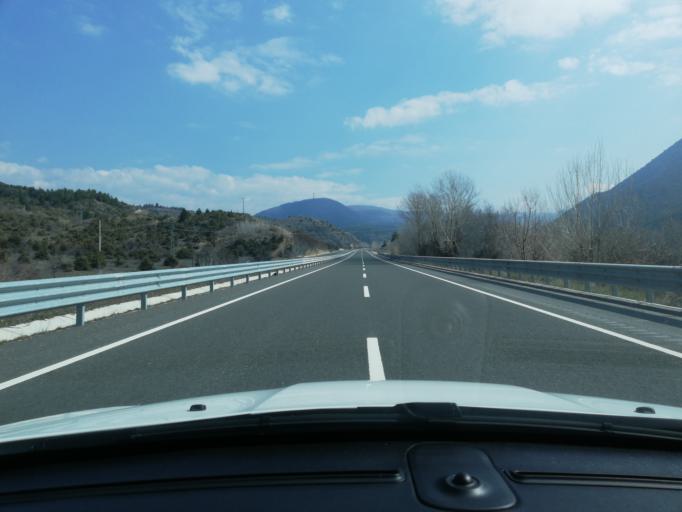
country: TR
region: Cankiri
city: Ilgaz
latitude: 40.9658
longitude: 33.6835
